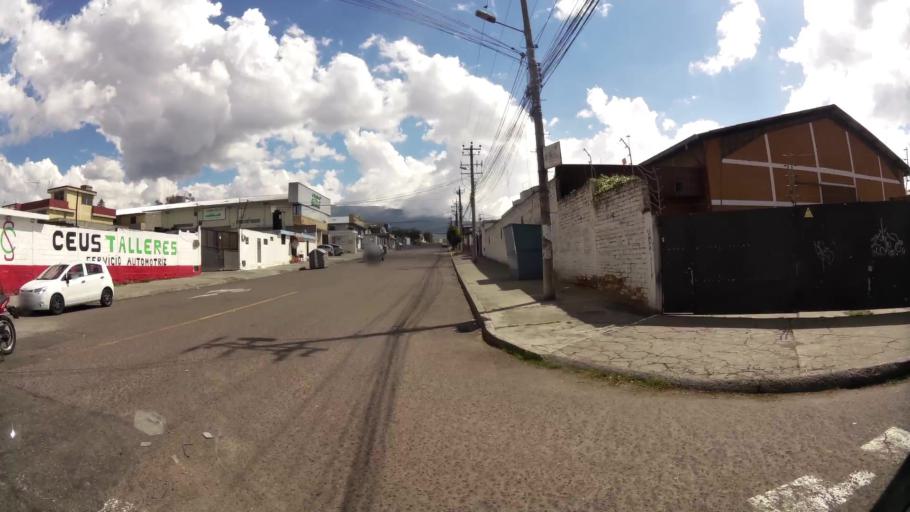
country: EC
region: Pichincha
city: Quito
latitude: -0.0980
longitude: -78.4741
